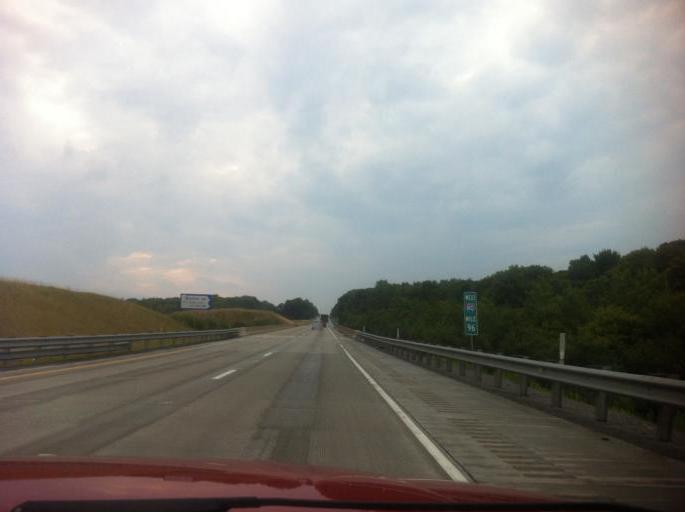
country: US
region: Pennsylvania
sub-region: Jefferson County
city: Falls Creek
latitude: 41.1497
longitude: -78.7967
